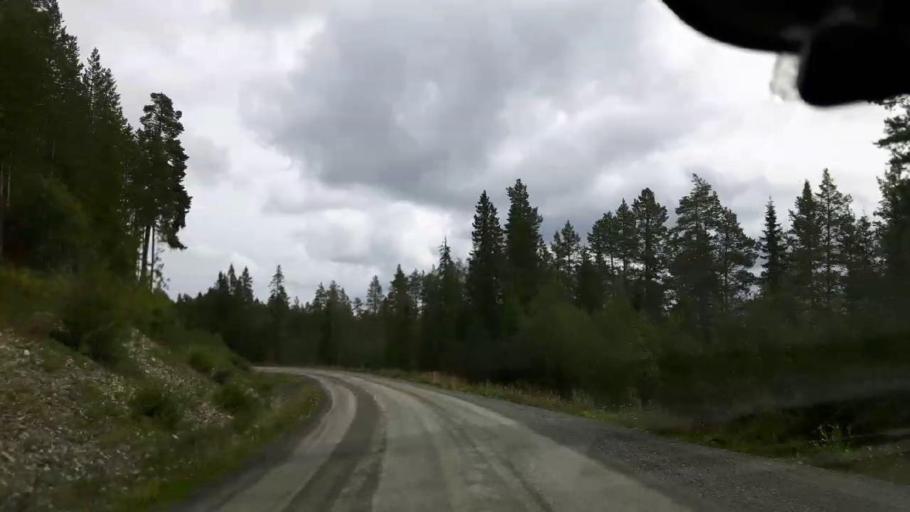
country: SE
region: Jaemtland
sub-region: Krokoms Kommun
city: Valla
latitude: 63.6102
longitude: 14.1090
